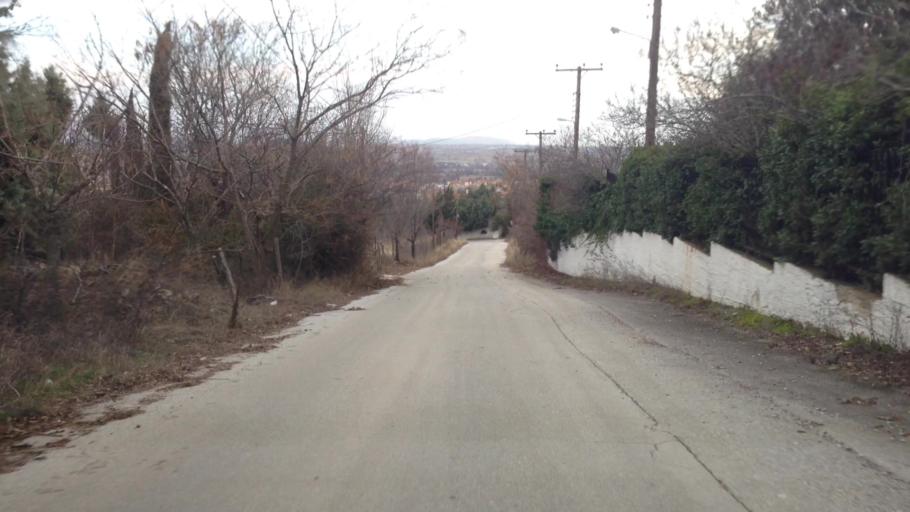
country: GR
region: West Macedonia
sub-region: Nomos Kozanis
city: Kozani
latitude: 40.2925
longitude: 21.7698
